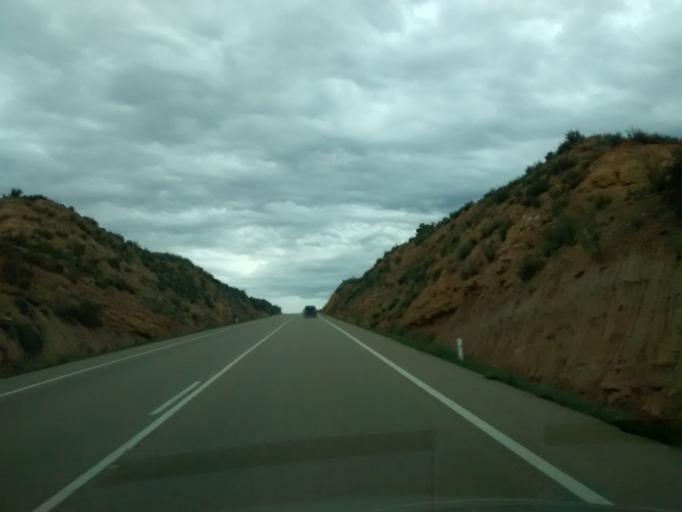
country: ES
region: Aragon
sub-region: Provincia de Zaragoza
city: Caspe
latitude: 41.2005
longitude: 0.0420
